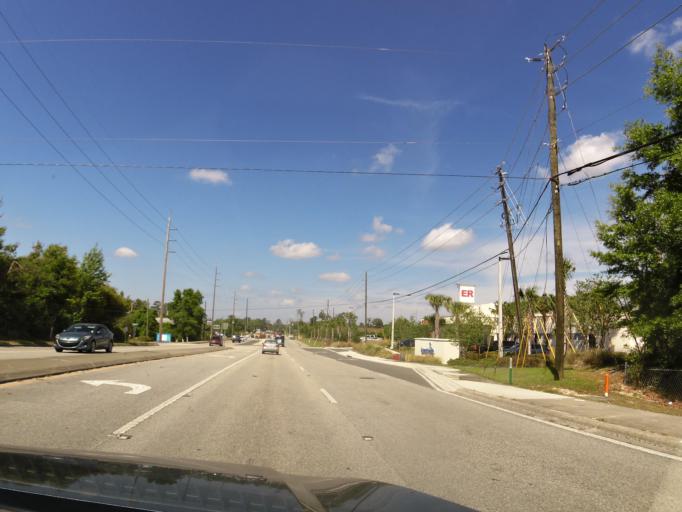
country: US
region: Florida
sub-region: Volusia County
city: Lake Helen
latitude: 28.9478
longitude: -81.2392
